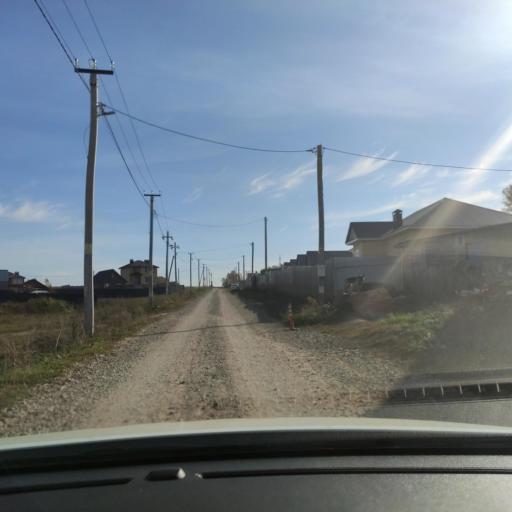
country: RU
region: Tatarstan
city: Vysokaya Gora
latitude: 55.7481
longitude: 49.4069
